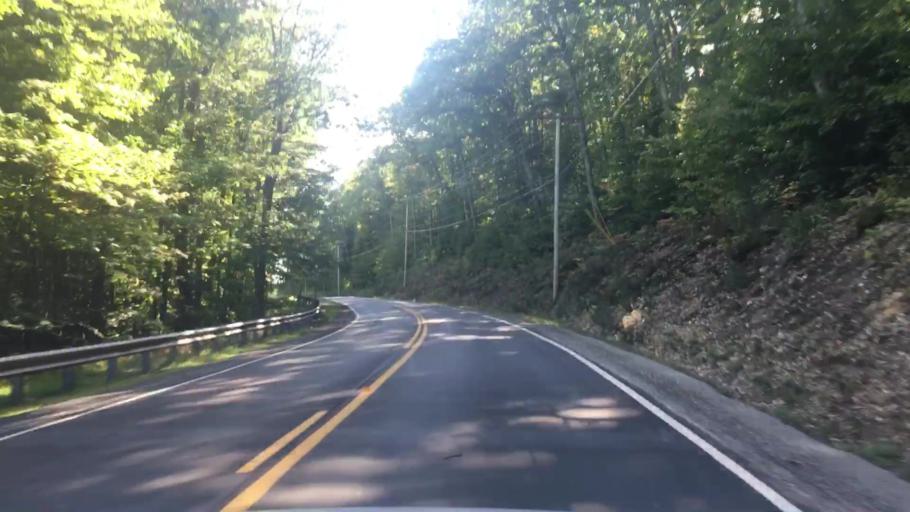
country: US
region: Maine
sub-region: Kennebec County
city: Mount Vernon
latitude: 44.4786
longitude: -70.0031
